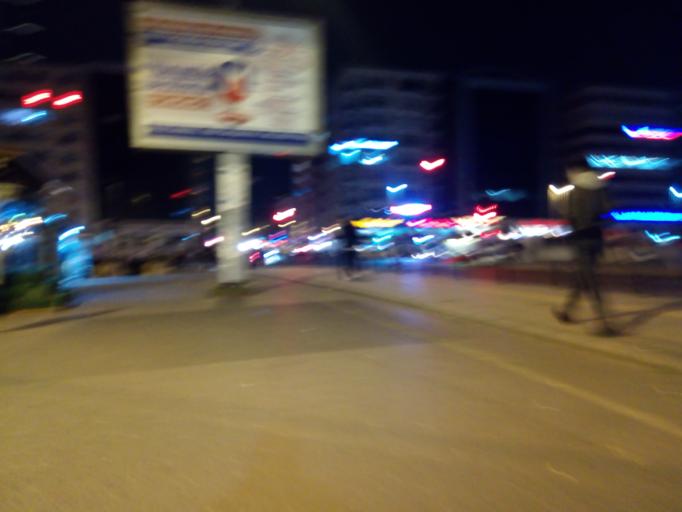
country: TR
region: Istanbul
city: Sisli
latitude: 41.0702
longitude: 28.9990
